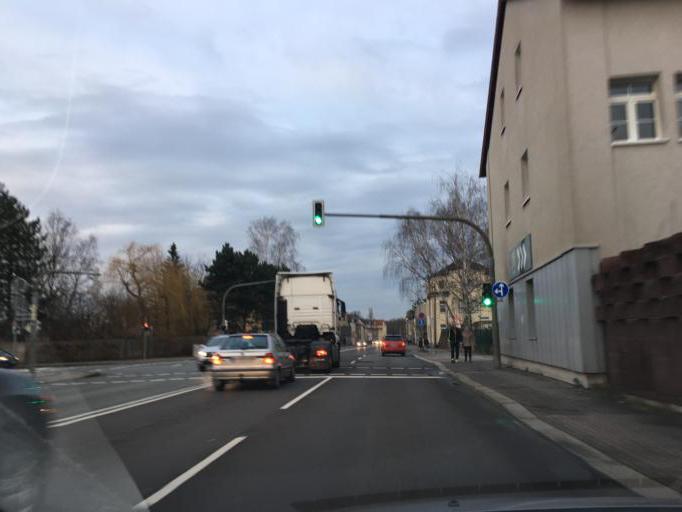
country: DE
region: Saxony
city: Borna
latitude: 51.1219
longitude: 12.4889
